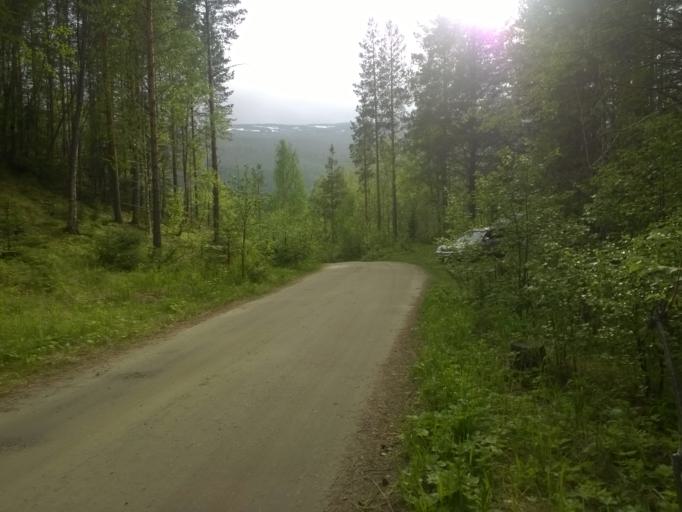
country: NO
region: Nordland
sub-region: Saltdal
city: Rognan
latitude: 66.8158
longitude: 15.3903
